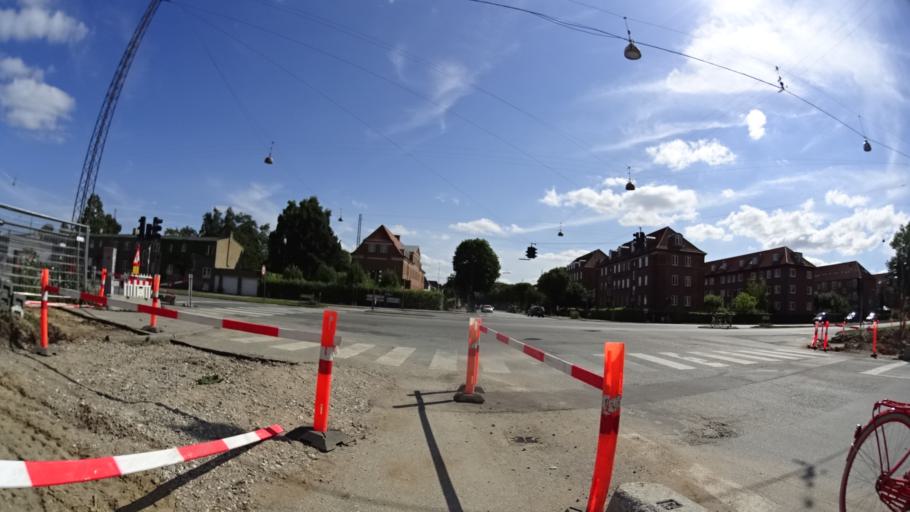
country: DK
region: Central Jutland
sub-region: Arhus Kommune
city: Arhus
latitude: 56.1407
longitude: 10.1946
